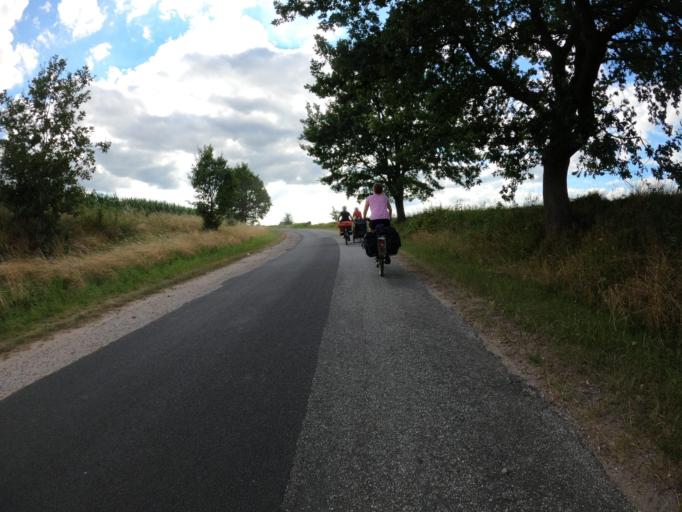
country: PL
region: West Pomeranian Voivodeship
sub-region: Powiat swidwinski
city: Swidwin
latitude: 53.7593
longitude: 15.6675
